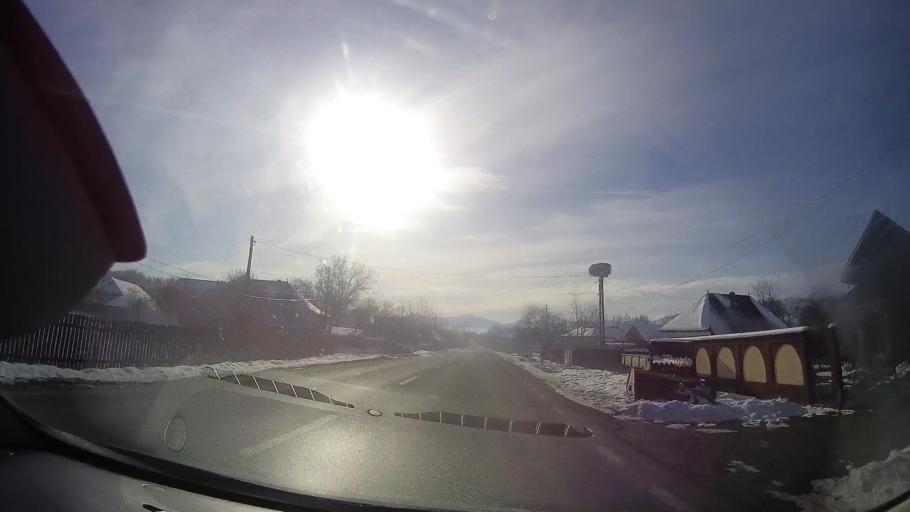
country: RO
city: Vanatori-Neamt
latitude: 47.1680
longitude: 26.3209
